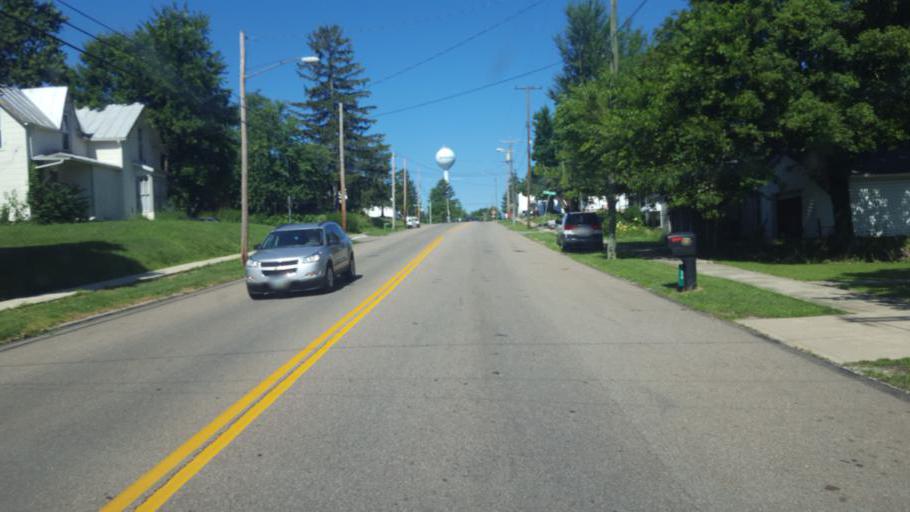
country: US
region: Ohio
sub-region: Morrow County
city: Cardington
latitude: 40.4021
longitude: -82.8089
